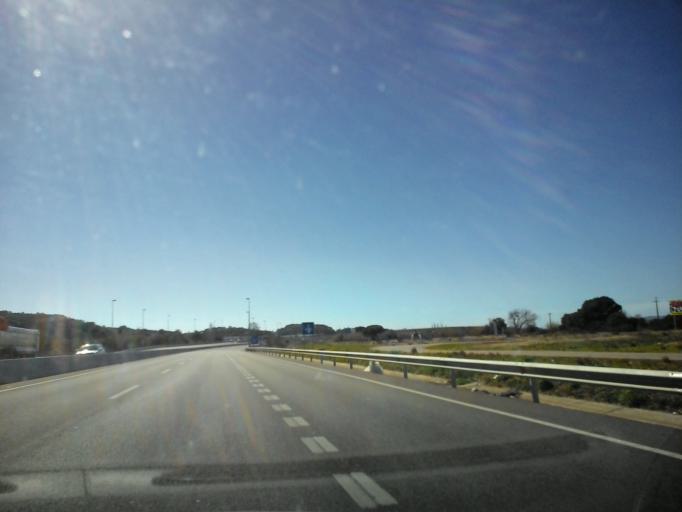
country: ES
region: Catalonia
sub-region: Provincia de Girona
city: Palamos
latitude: 41.8694
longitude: 3.1378
